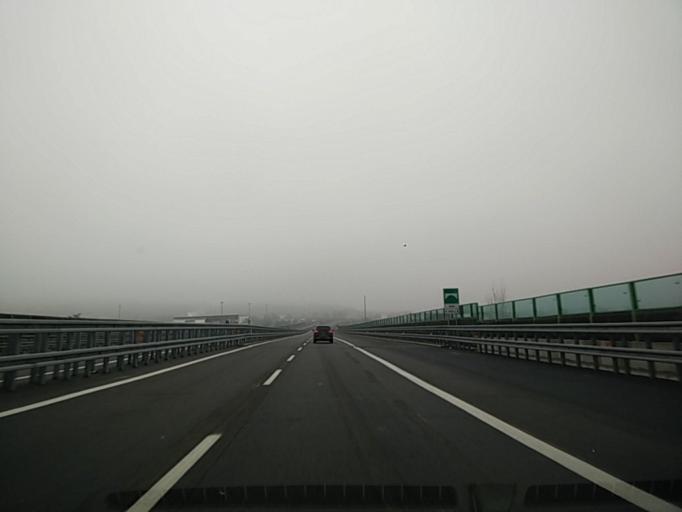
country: IT
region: Piedmont
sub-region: Provincia di Asti
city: Asti
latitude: 44.9148
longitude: 8.2180
